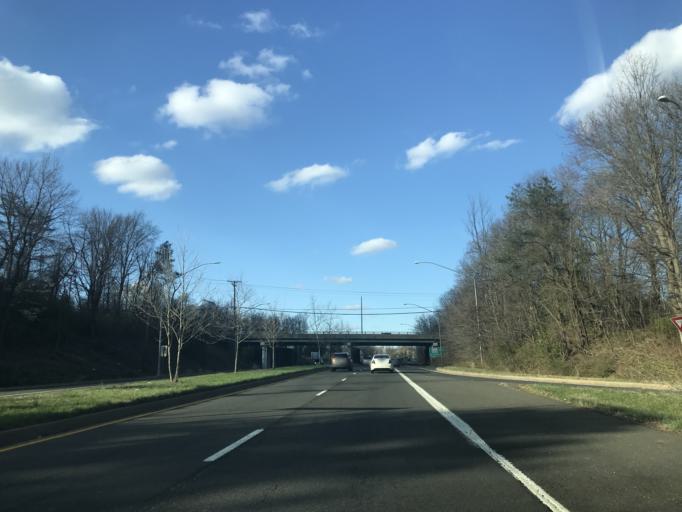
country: US
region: Maryland
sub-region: Prince George's County
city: Glenarden
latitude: 38.9249
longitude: -76.8751
